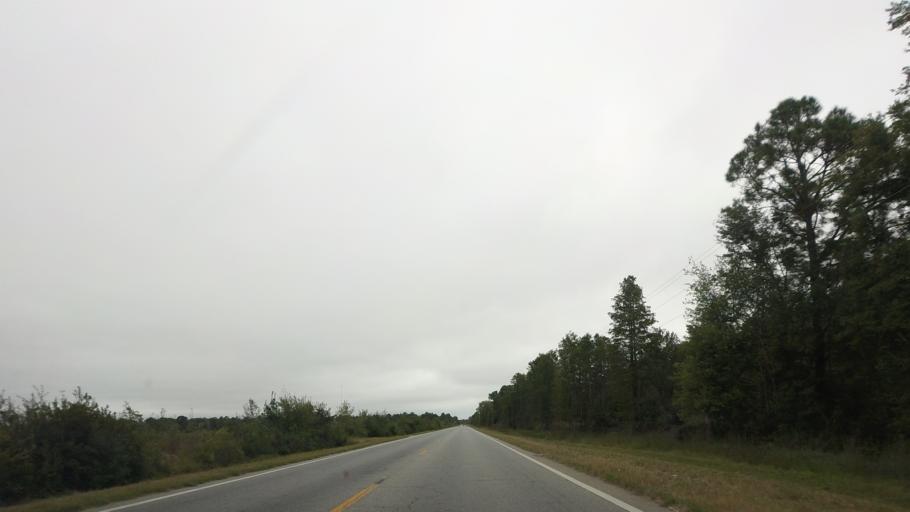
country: US
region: Georgia
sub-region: Berrien County
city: Nashville
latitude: 31.1636
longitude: -83.2277
